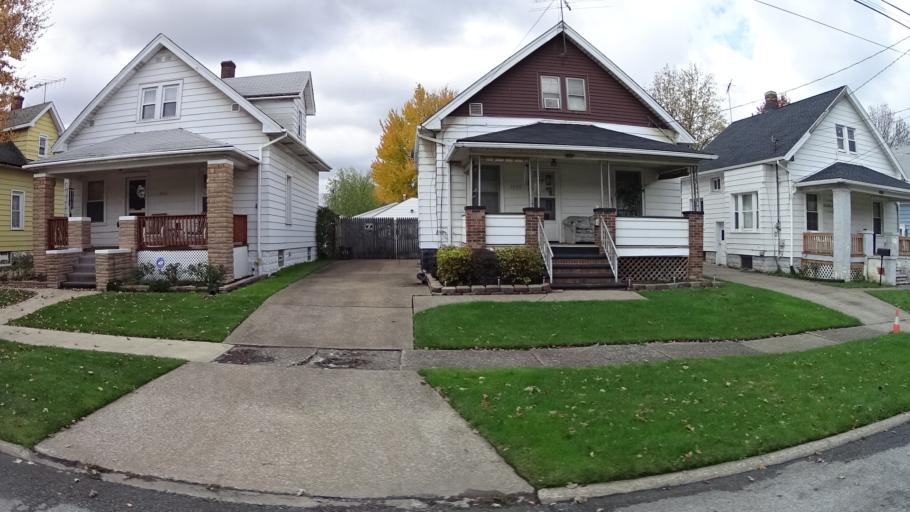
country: US
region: Ohio
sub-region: Lorain County
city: Lorain
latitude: 41.4461
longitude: -82.1593
